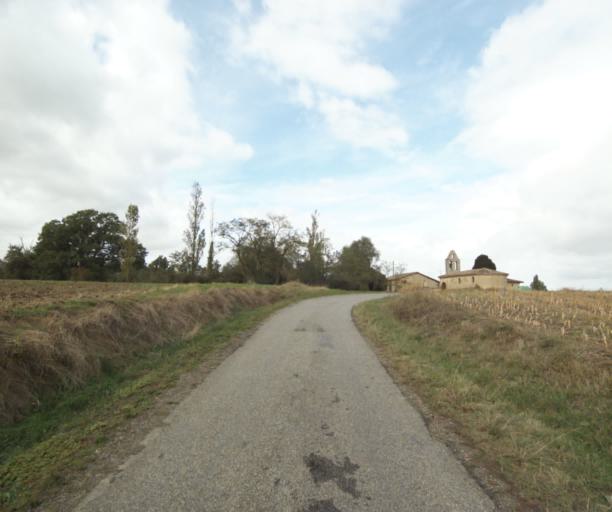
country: FR
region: Midi-Pyrenees
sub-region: Departement du Tarn-et-Garonne
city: Beaumont-de-Lomagne
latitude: 43.8768
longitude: 1.0824
